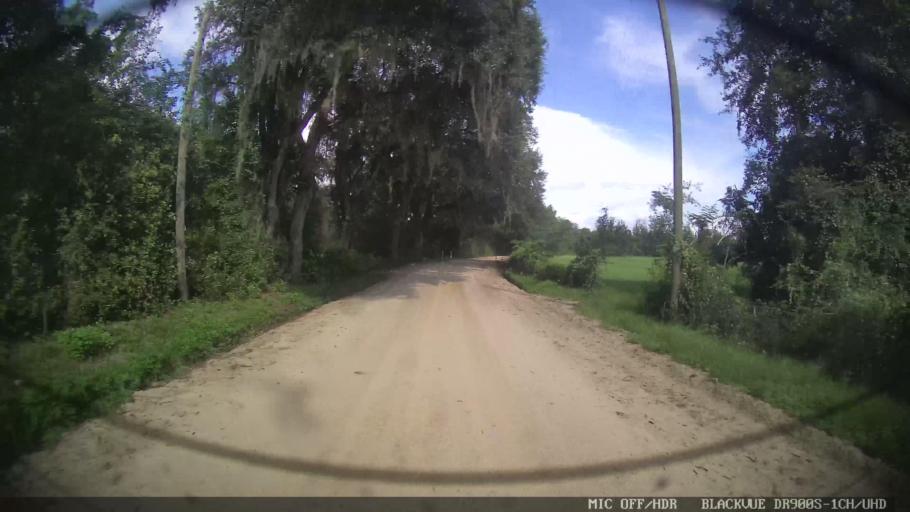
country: US
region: Georgia
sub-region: Echols County
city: Statenville
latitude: 30.6324
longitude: -83.1948
